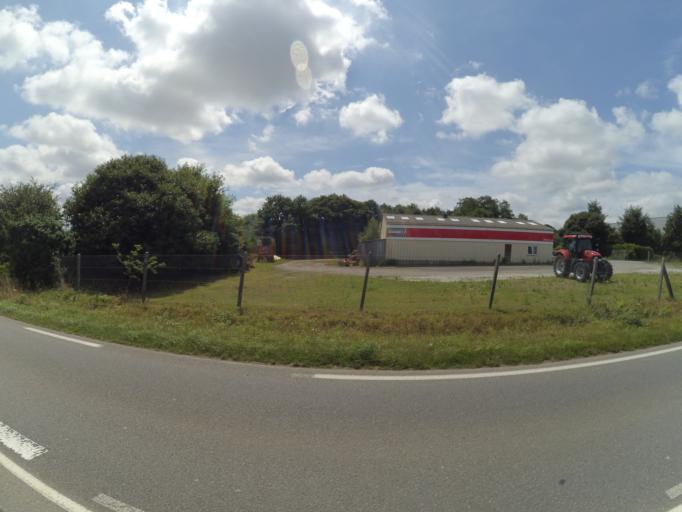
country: FR
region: Brittany
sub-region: Departement du Finistere
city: Ergue-Gaberic
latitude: 47.9723
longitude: -3.9868
